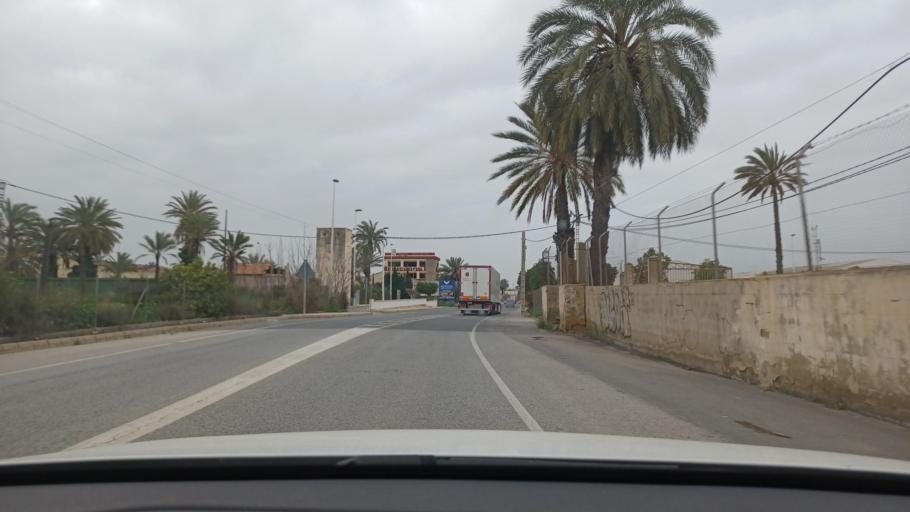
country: ES
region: Valencia
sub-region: Provincia de Alicante
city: Elche
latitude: 38.2482
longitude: -0.7049
